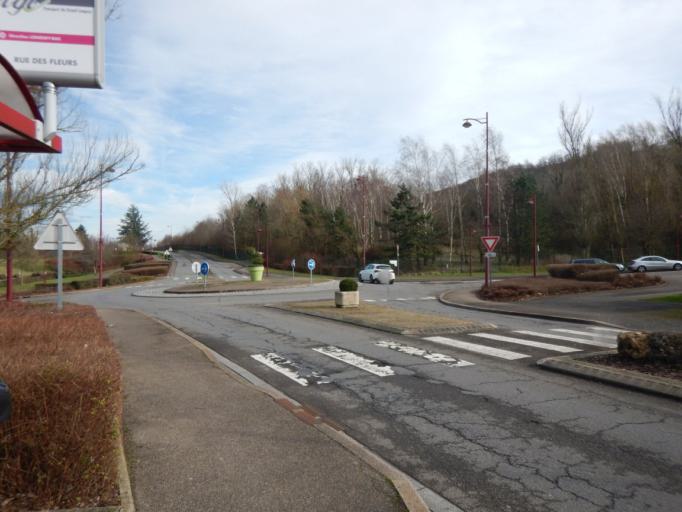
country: FR
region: Lorraine
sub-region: Departement de Meurthe-et-Moselle
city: Longlaville
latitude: 49.5374
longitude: 5.8074
